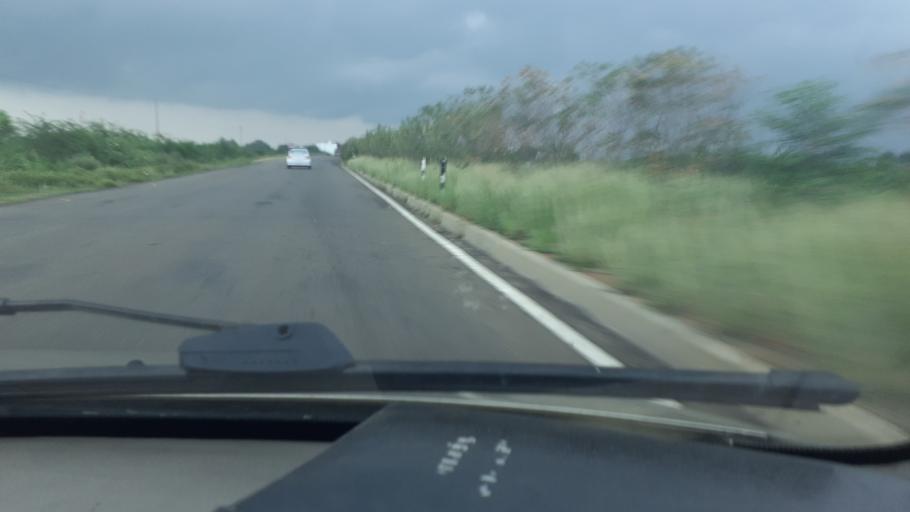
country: IN
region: Tamil Nadu
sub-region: Thoothukkudi
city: Kovilpatti
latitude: 9.1178
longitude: 77.8153
